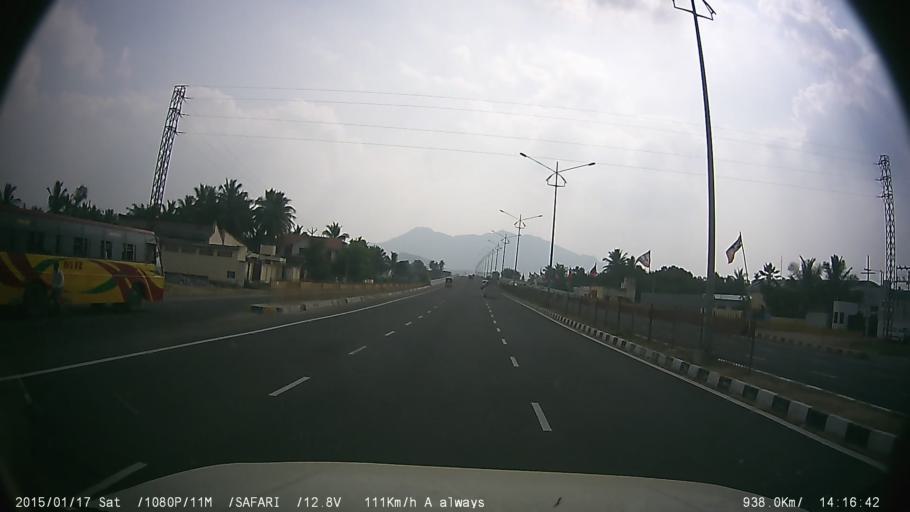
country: IN
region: Tamil Nadu
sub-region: Vellore
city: Ambur
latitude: 12.7504
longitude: 78.6981
